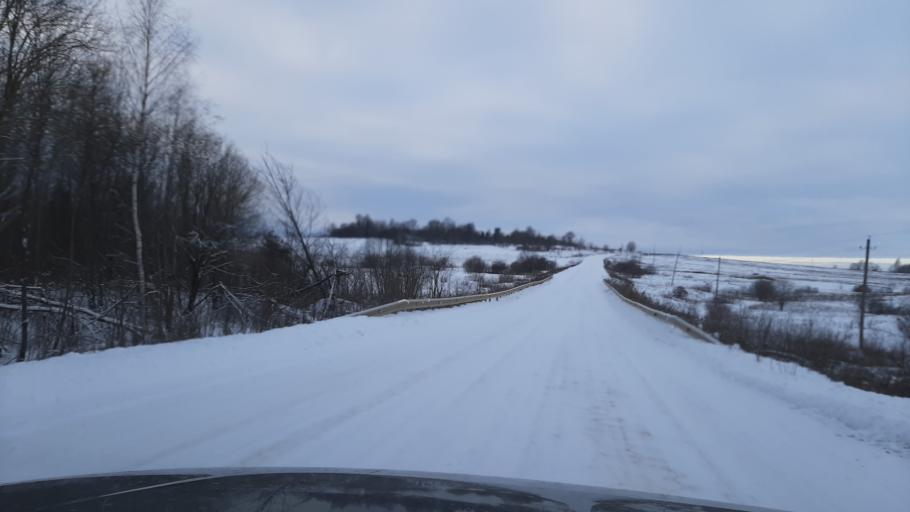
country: RU
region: Kostroma
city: Volgorechensk
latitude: 57.4444
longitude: 40.9464
